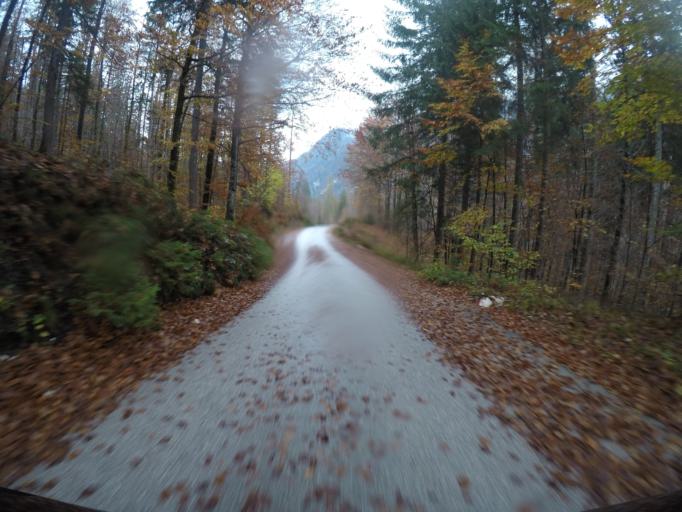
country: SI
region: Kranjska Gora
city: Mojstrana
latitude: 46.4310
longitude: 13.8762
